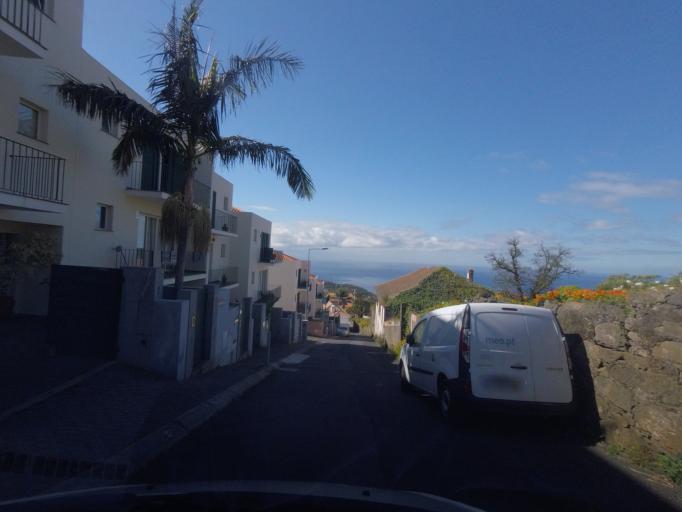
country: PT
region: Madeira
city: Camara de Lobos
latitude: 32.6654
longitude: -16.9754
